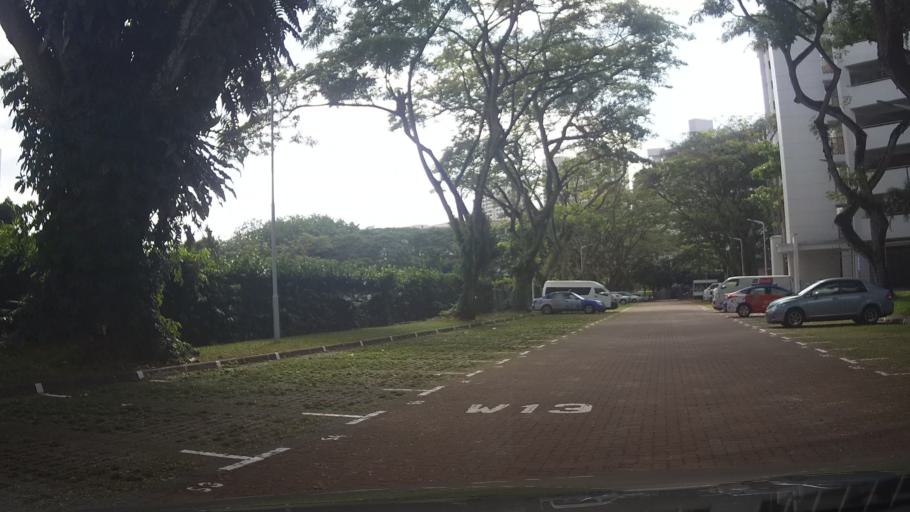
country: MY
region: Johor
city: Johor Bahru
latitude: 1.4448
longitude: 103.7741
